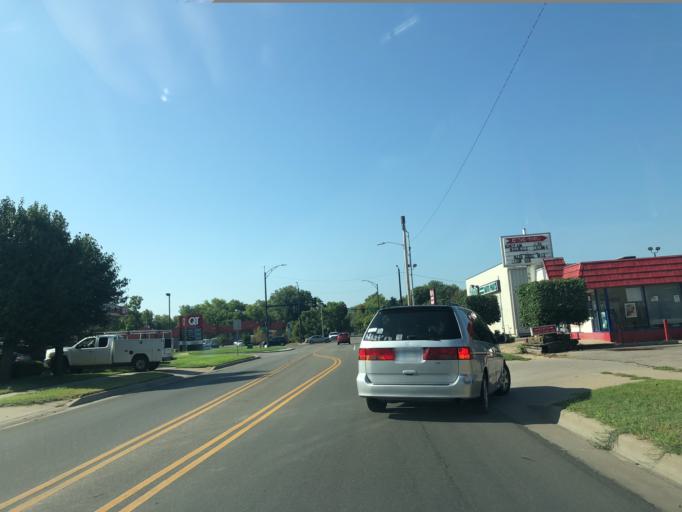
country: US
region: Kansas
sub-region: Sedgwick County
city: Wichita
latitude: 37.7236
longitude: -97.3448
